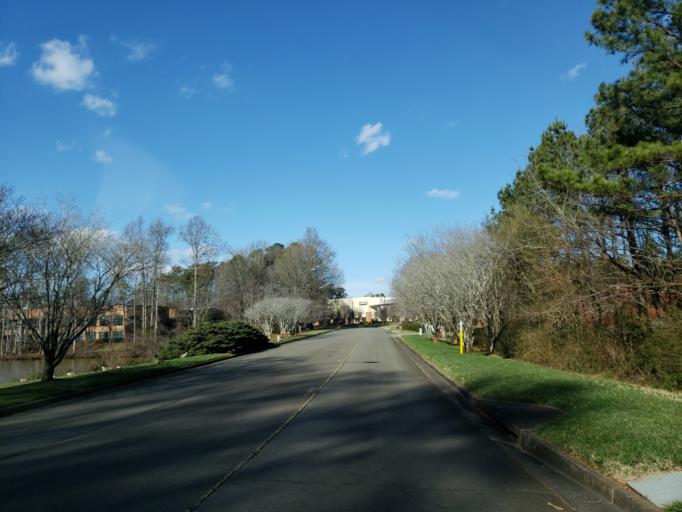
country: US
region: Georgia
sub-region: Cobb County
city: Marietta
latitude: 33.9875
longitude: -84.5209
